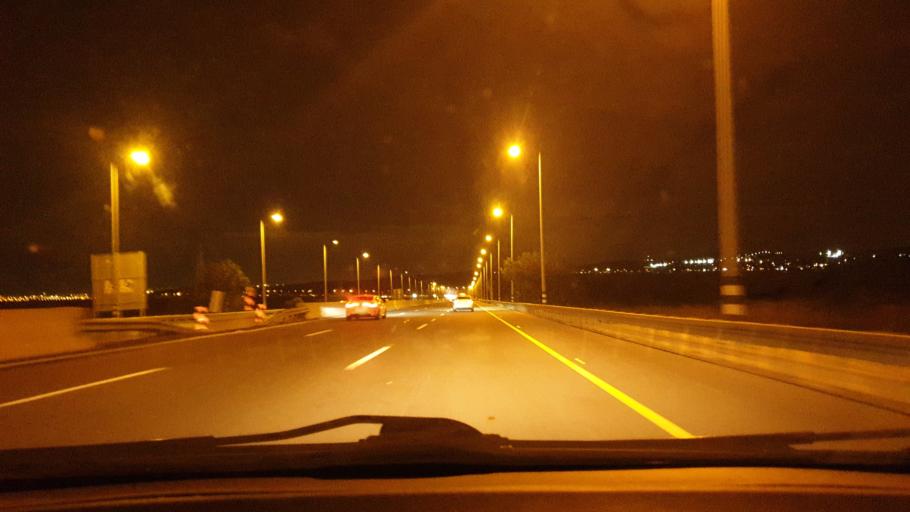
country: IL
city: Nof Ayalon
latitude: 31.8500
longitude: 34.9838
